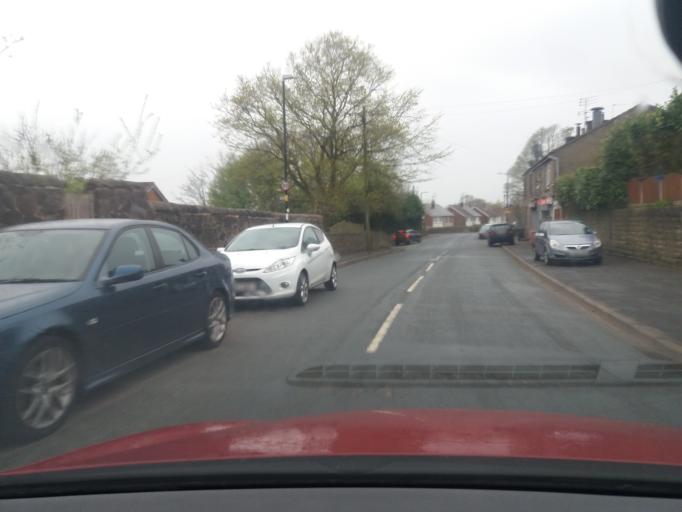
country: GB
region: England
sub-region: Lancashire
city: Clayton-le-Woods
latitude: 53.6893
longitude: -2.6366
